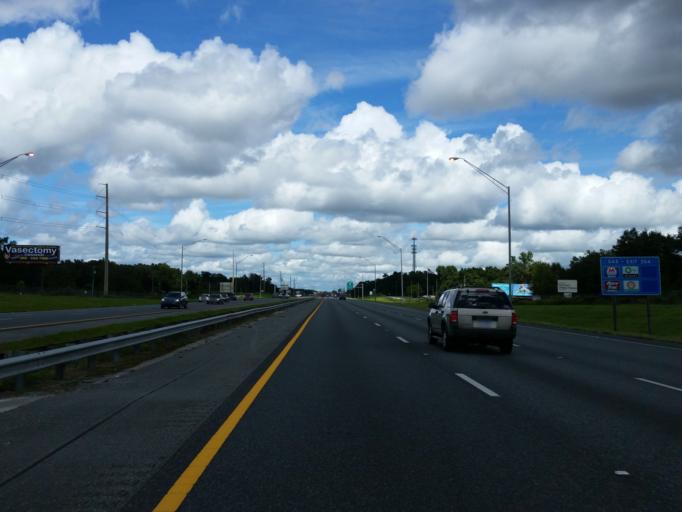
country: US
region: Florida
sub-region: Marion County
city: Ocala
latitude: 29.1918
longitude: -82.1847
